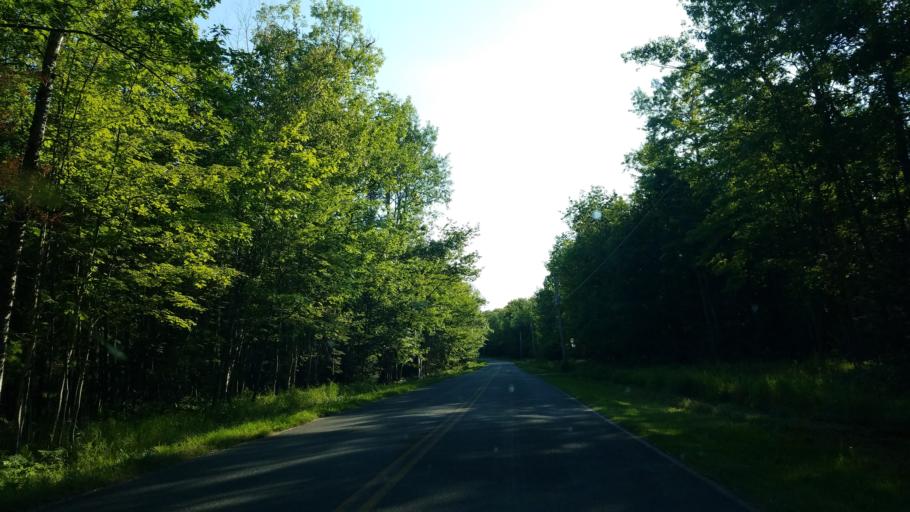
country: US
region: Wisconsin
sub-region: Bayfield County
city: Washburn
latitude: 46.7774
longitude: -90.7314
